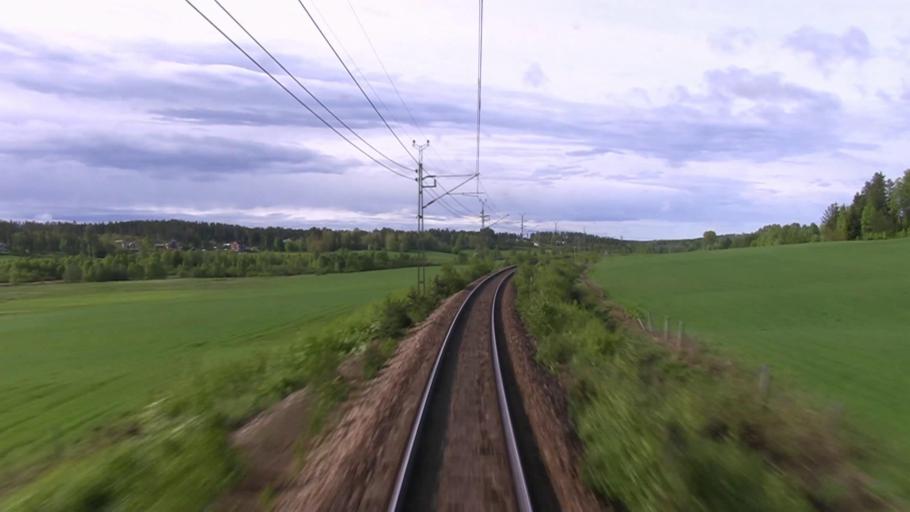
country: SE
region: Vaesterbotten
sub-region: Vindelns Kommun
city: Vindeln
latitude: 64.1063
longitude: 19.6844
